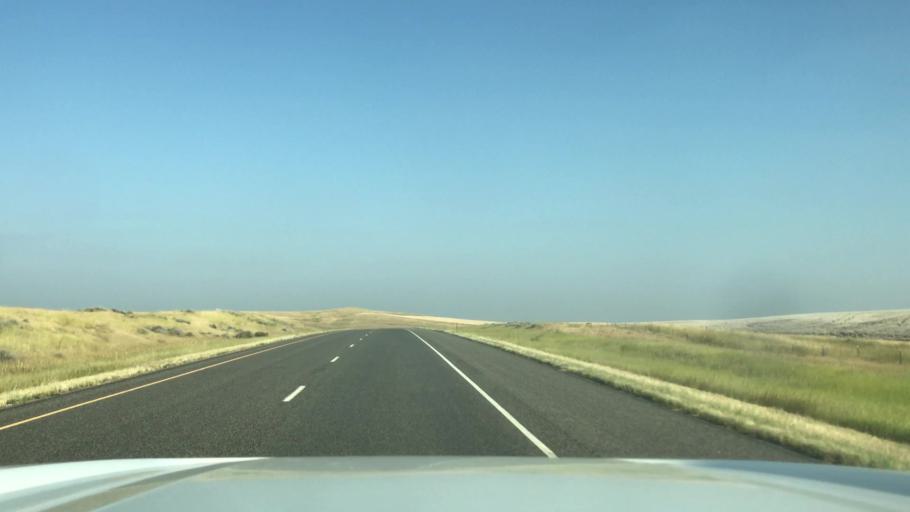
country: US
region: Montana
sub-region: Big Horn County
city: Hardin
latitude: 45.7704
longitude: -107.9338
